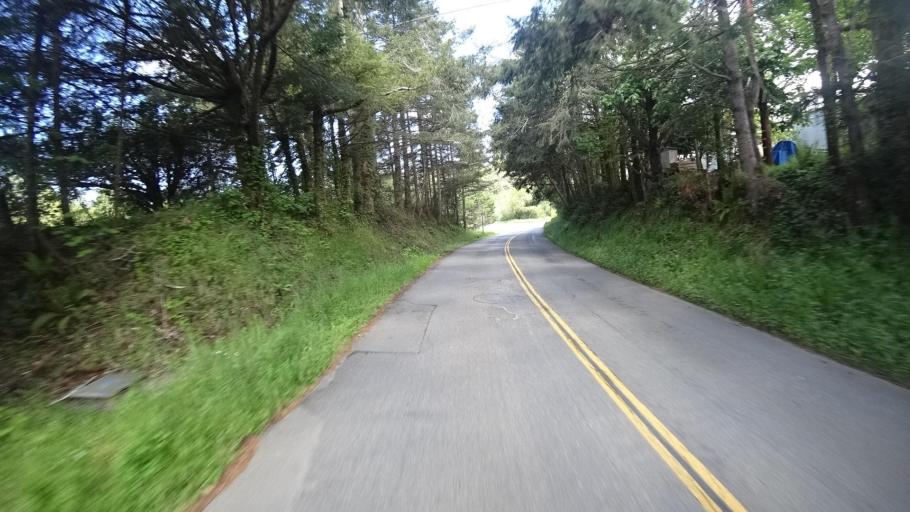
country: US
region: California
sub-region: Humboldt County
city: Blue Lake
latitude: 40.9016
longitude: -124.0282
